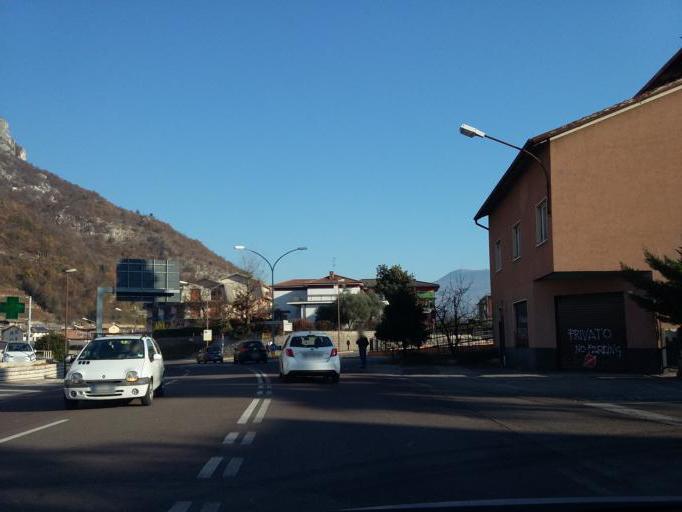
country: IT
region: Trentino-Alto Adige
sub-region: Provincia di Trento
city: Mori
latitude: 45.8517
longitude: 10.9791
